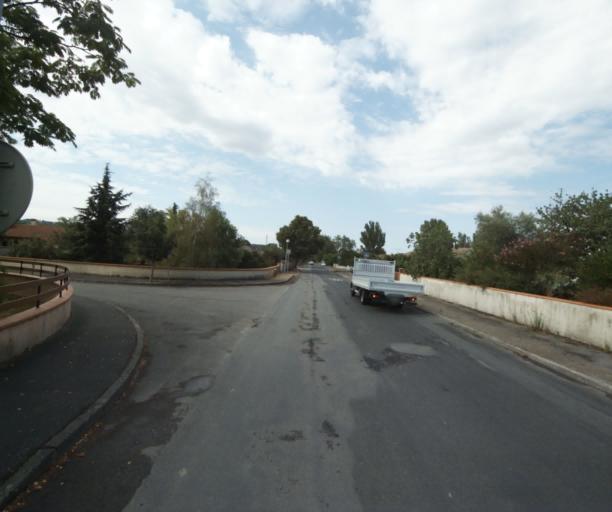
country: FR
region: Midi-Pyrenees
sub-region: Departement de la Haute-Garonne
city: Revel
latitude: 43.4618
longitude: 1.9942
